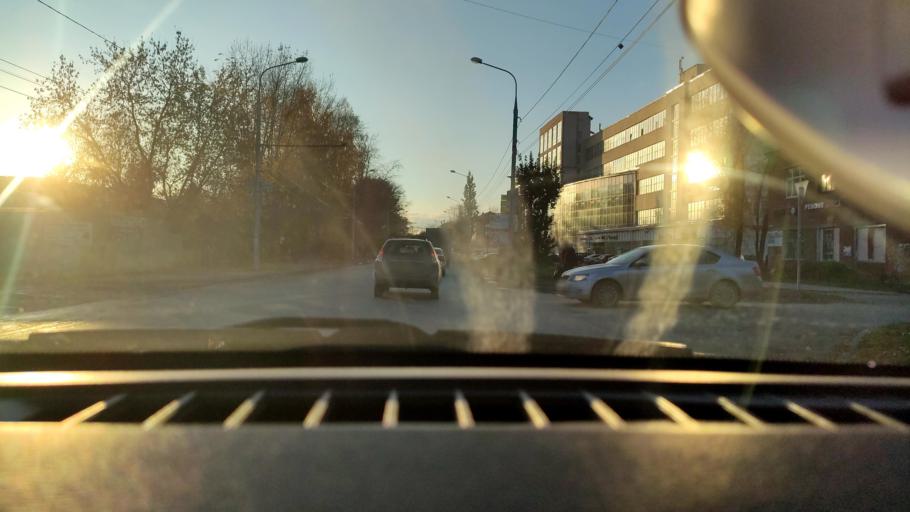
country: RU
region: Perm
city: Perm
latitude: 57.9662
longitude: 56.2406
